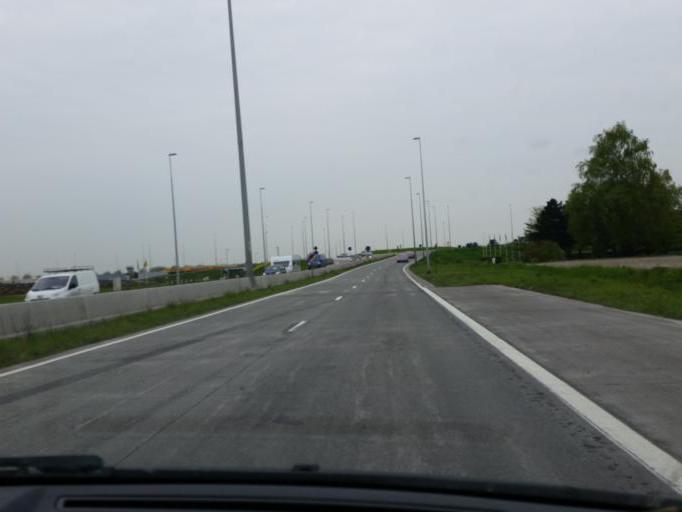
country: BE
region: Flanders
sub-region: Provincie Oost-Vlaanderen
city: Zelzate
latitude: 51.1854
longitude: 3.8330
